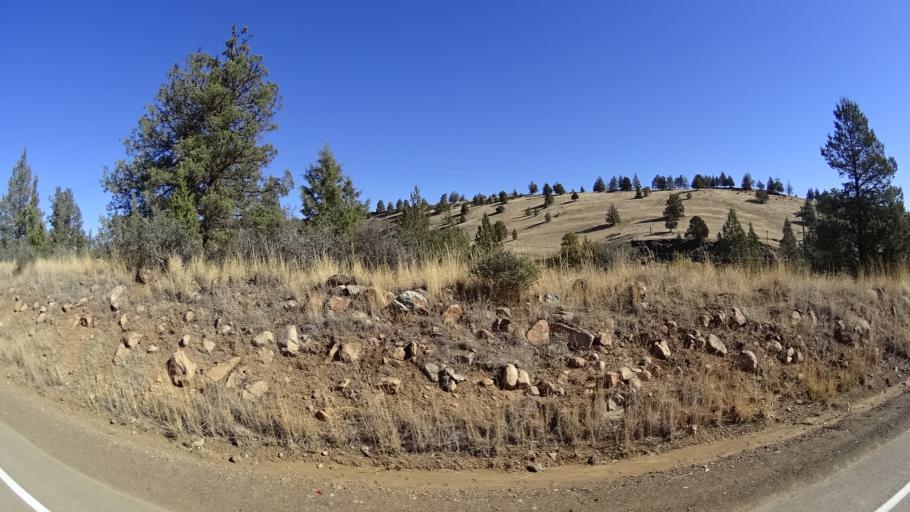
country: US
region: California
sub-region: Siskiyou County
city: Montague
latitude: 41.8690
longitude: -122.4708
